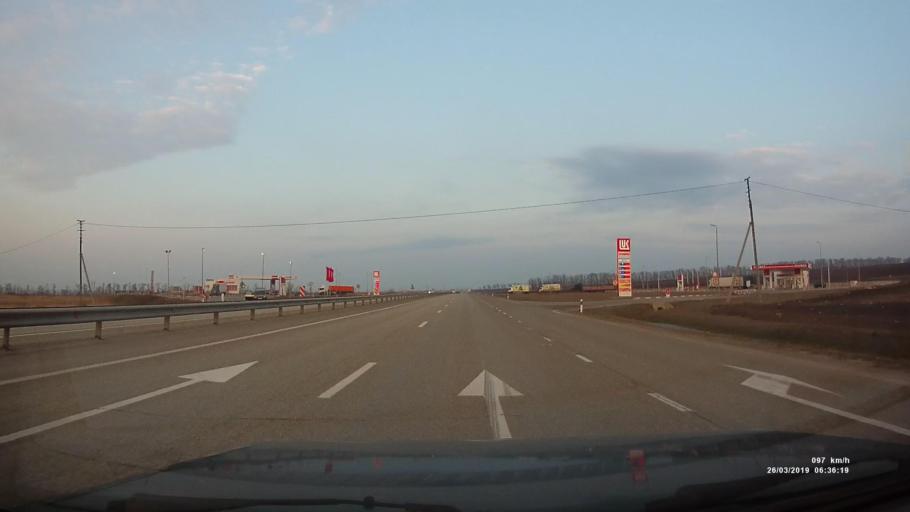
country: RU
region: Rostov
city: Chaltyr
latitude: 47.2834
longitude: 39.4268
